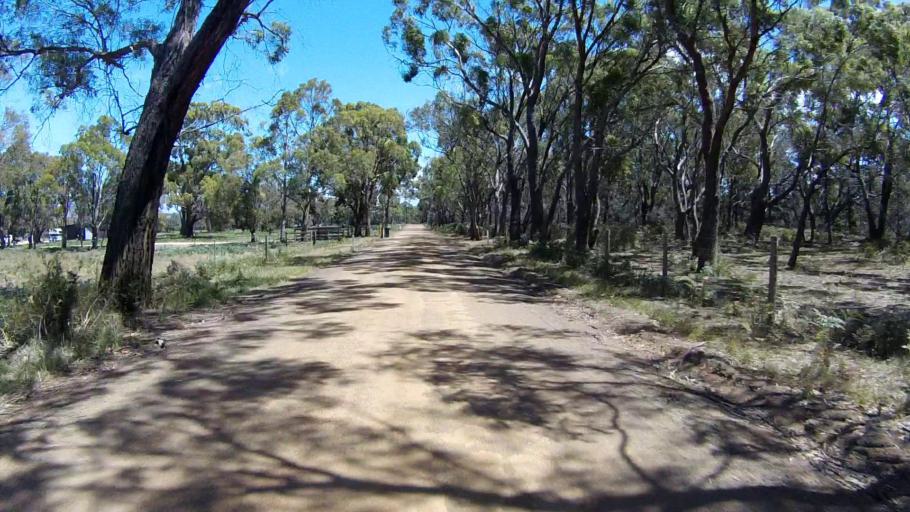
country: AU
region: Tasmania
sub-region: Clarence
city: Sandford
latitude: -42.9327
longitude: 147.5160
